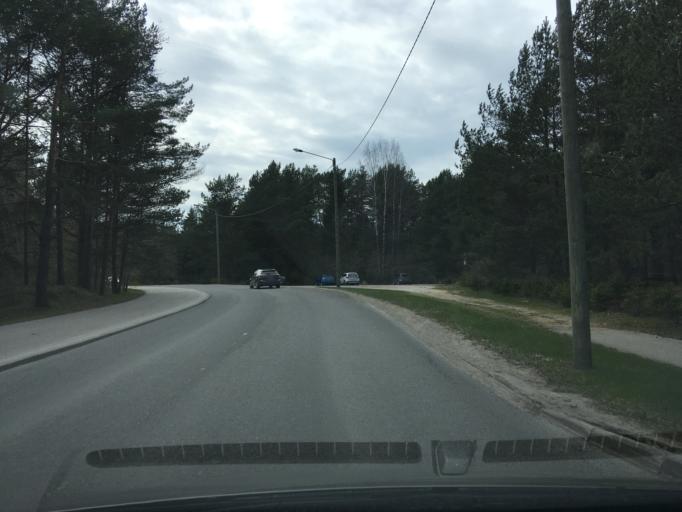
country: EE
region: Harju
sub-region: Tallinna linn
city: Kose
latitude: 59.4728
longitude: 24.9118
